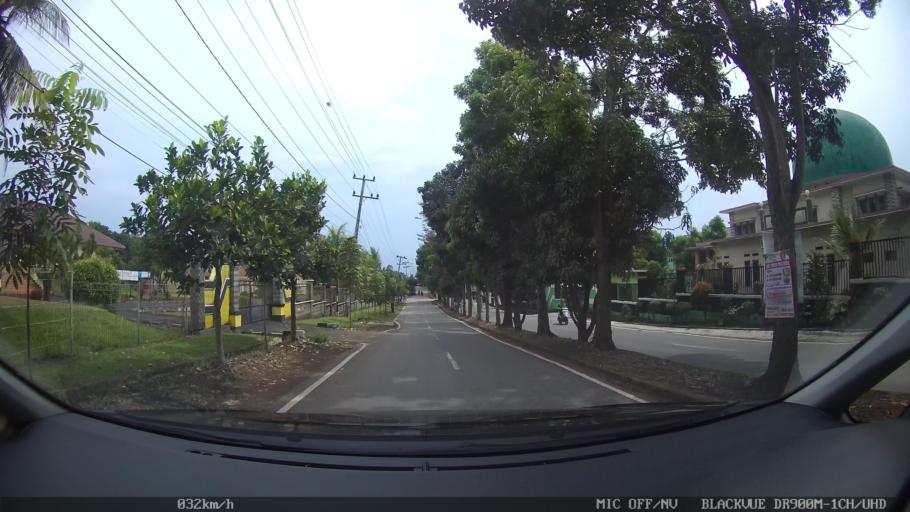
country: ID
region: Lampung
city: Bandarlampung
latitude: -5.4044
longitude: 105.2006
